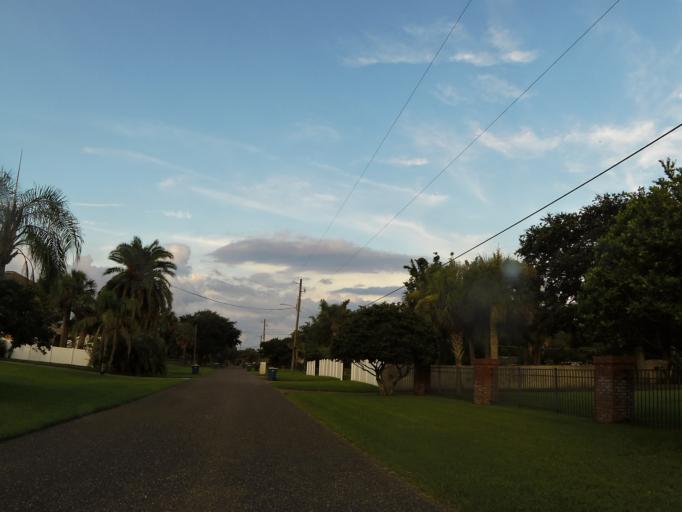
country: US
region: Florida
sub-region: Duval County
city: Atlantic Beach
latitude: 30.3936
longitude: -81.4984
